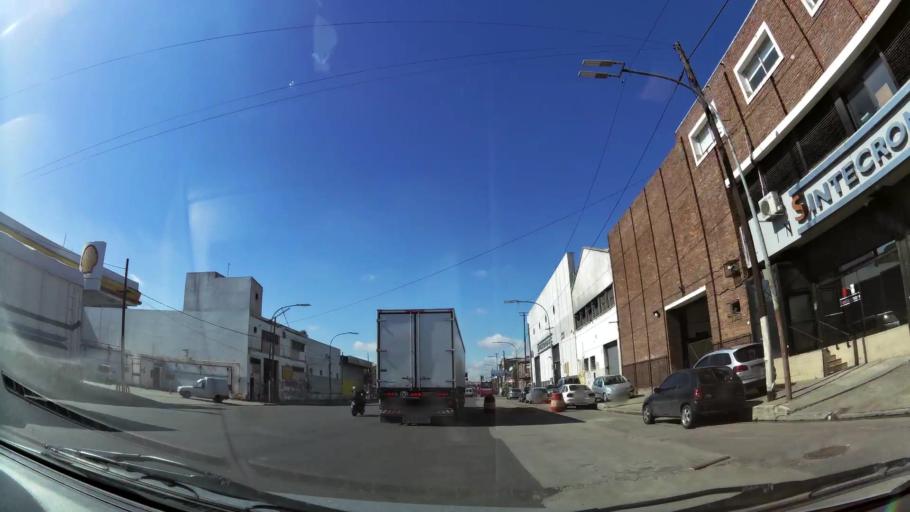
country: AR
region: Buenos Aires
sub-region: Partido de Lanus
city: Lanus
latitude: -34.6658
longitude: -58.4177
